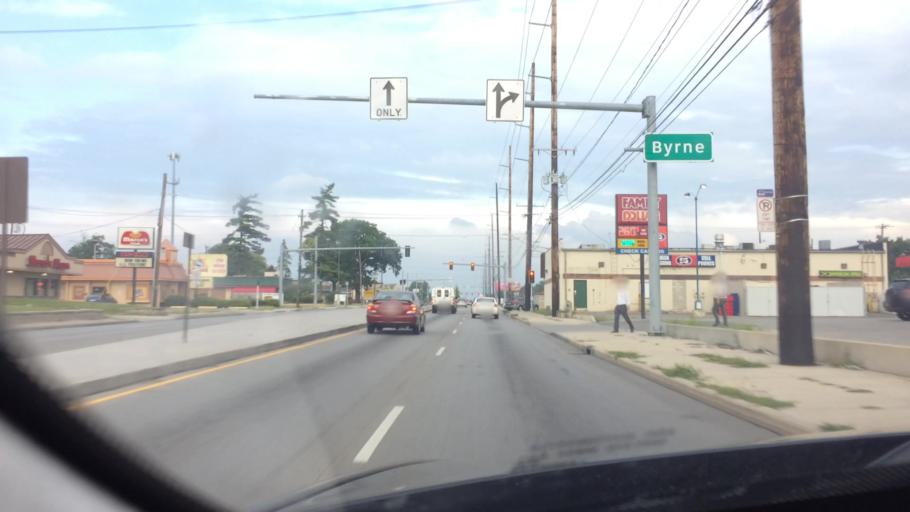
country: US
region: Ohio
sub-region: Lucas County
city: Ottawa Hills
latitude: 41.6527
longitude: -83.6273
